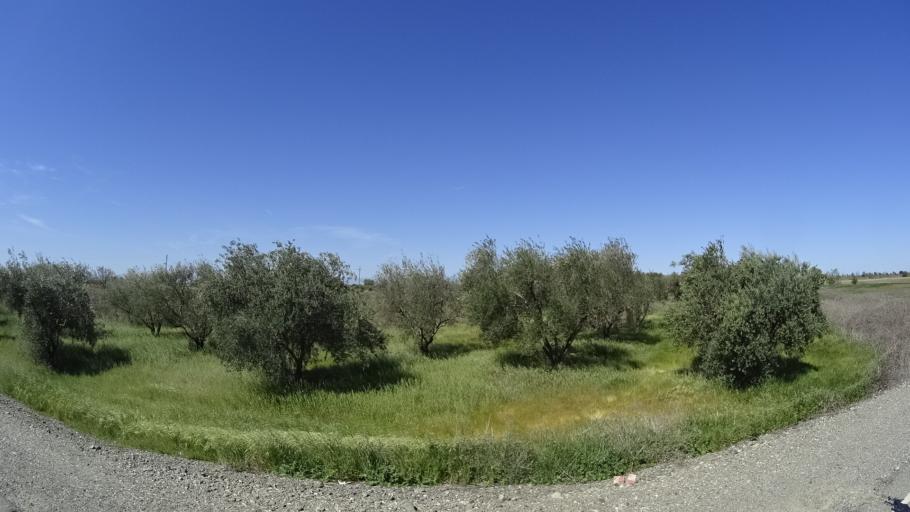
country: US
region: California
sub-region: Glenn County
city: Hamilton City
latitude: 39.7443
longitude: -122.1046
